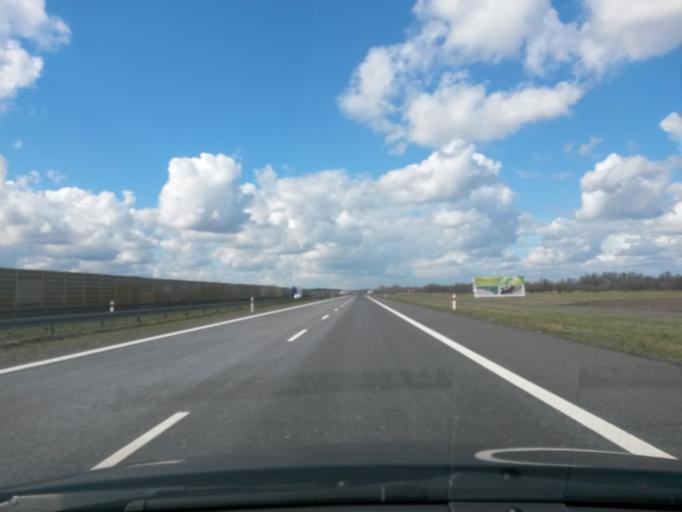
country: PL
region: Greater Poland Voivodeship
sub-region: Powiat kolski
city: Dabie
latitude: 52.0497
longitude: 18.8496
